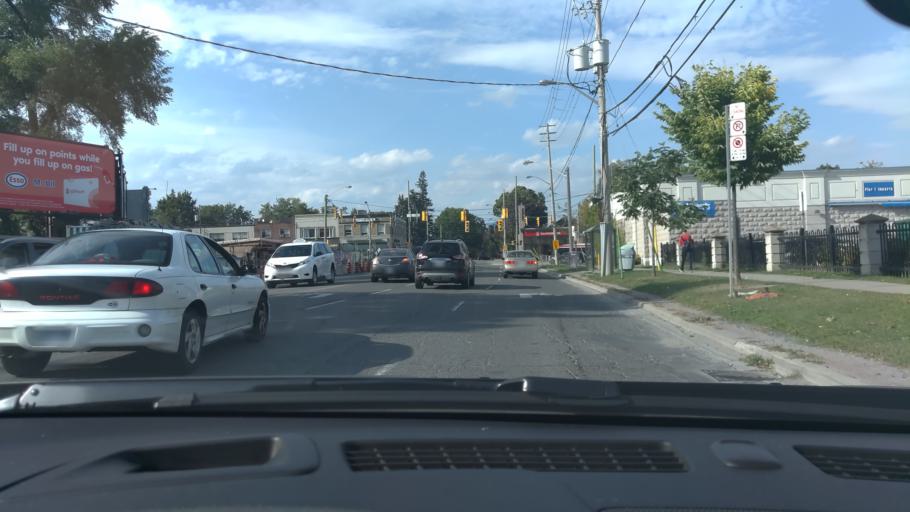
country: CA
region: Ontario
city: Toronto
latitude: 43.7127
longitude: -79.3644
